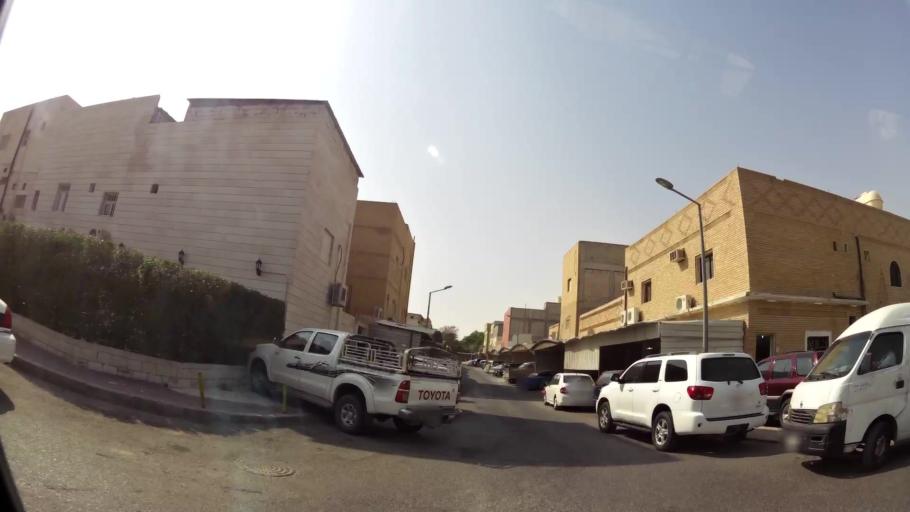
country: KW
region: Muhafazat al Jahra'
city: Al Jahra'
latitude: 29.3395
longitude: 47.6584
